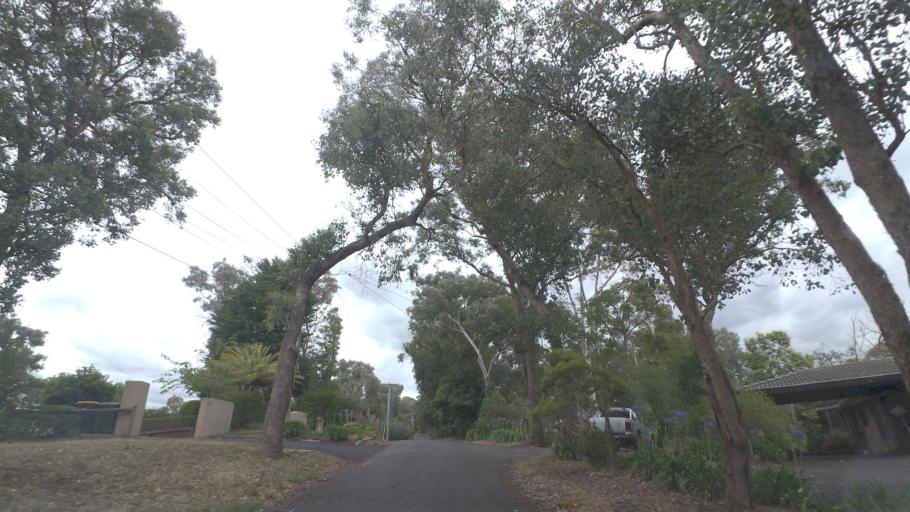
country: AU
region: Victoria
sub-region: Manningham
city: Warrandyte
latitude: -37.7553
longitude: 145.2160
